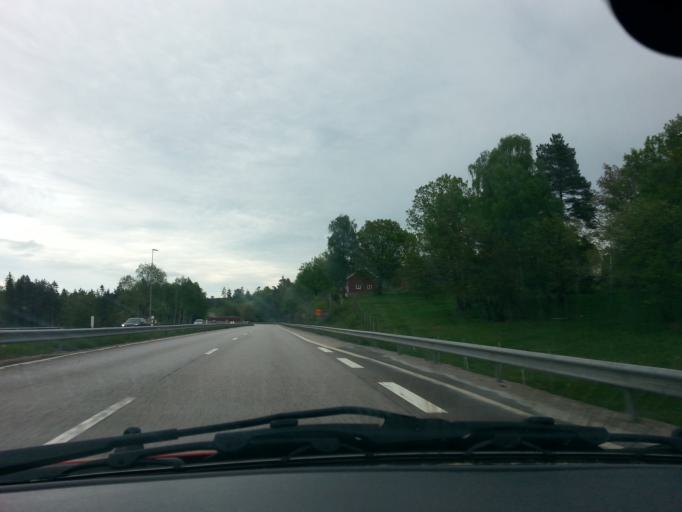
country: SE
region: Vaestra Goetaland
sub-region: Alingsas Kommun
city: Ingared
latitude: 57.8702
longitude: 12.4910
